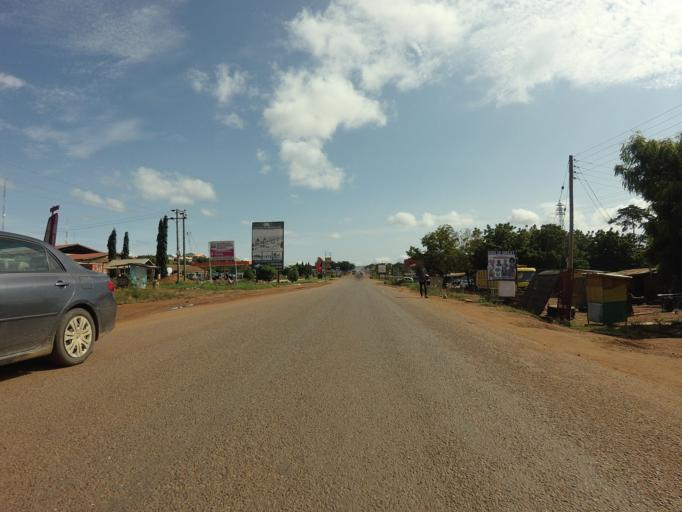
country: GH
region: Eastern
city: Aburi
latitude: 5.8091
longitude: -0.1238
